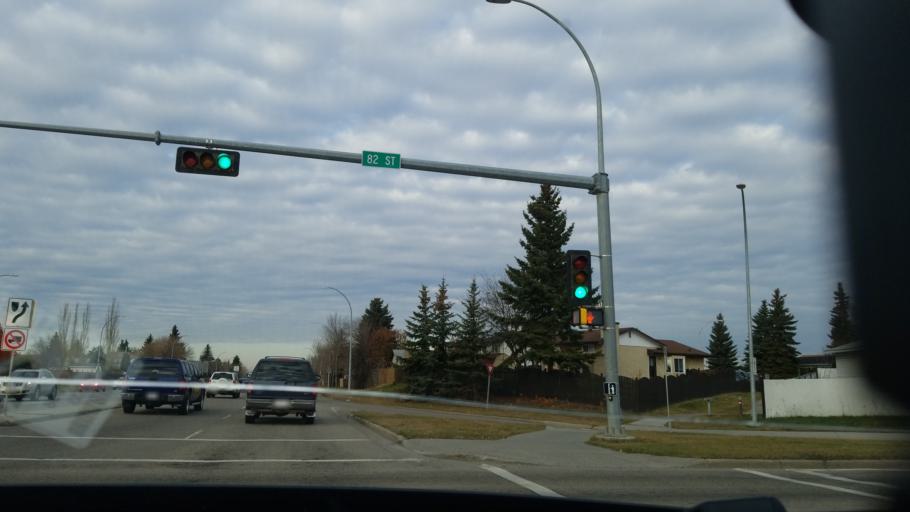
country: CA
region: Alberta
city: Edmonton
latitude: 53.6160
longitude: -113.4675
